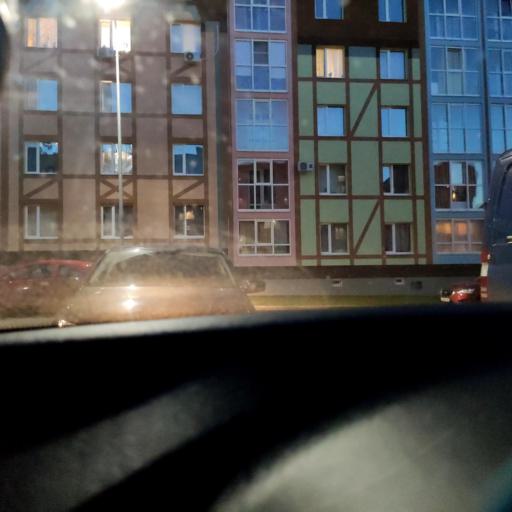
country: RU
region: Samara
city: Petra-Dubrava
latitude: 53.2978
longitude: 50.3269
